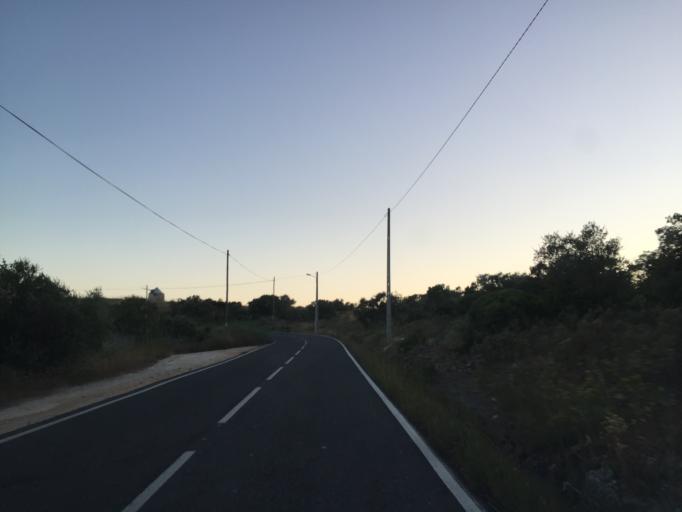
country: PT
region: Santarem
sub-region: Ourem
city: Fatima
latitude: 39.6229
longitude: -8.6465
